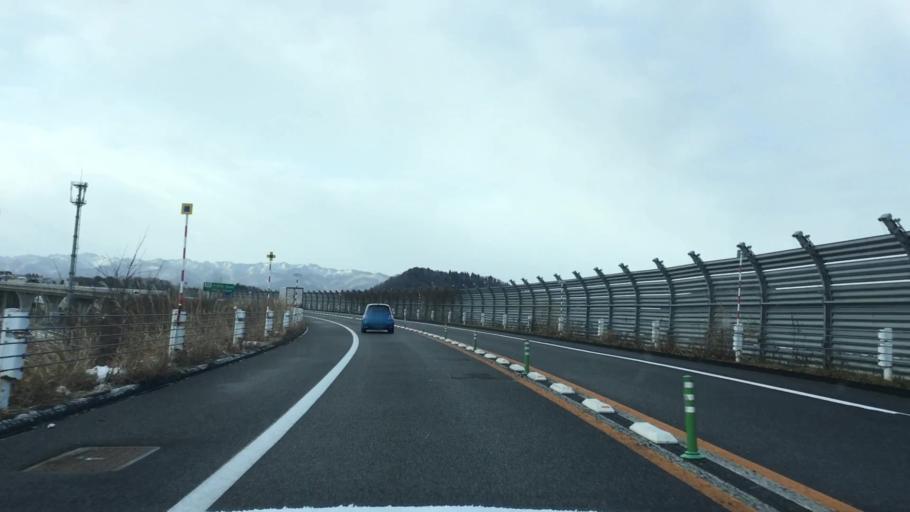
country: JP
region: Akita
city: Odate
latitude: 40.2883
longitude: 140.5428
